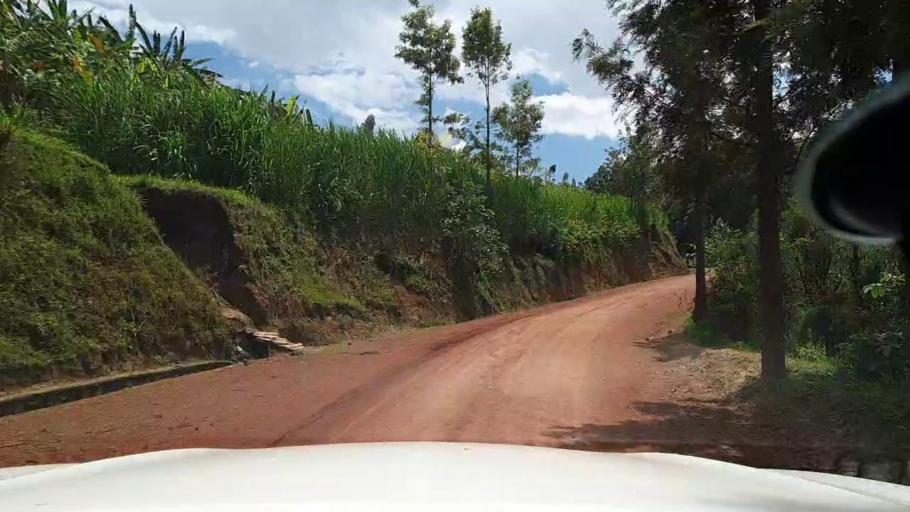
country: RW
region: Northern Province
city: Byumba
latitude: -1.7525
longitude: 29.8505
